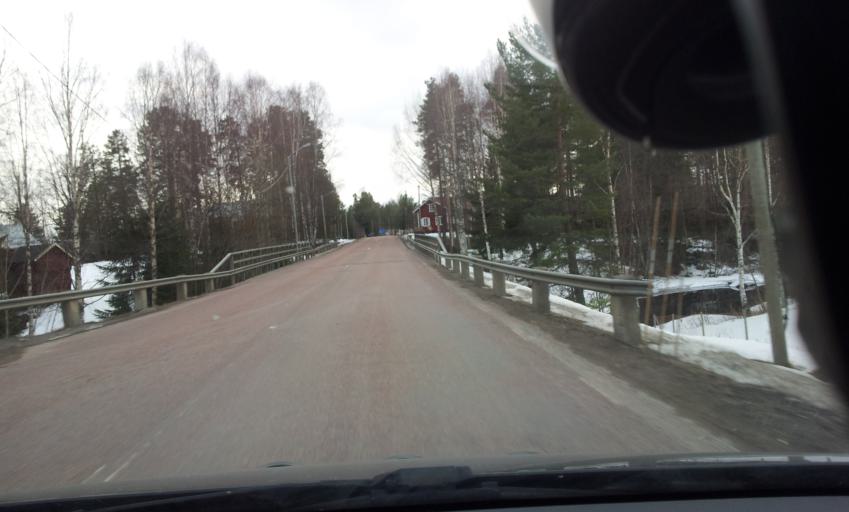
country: SE
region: Vaesternorrland
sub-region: Ange Kommun
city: Ange
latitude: 62.1880
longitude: 15.6584
